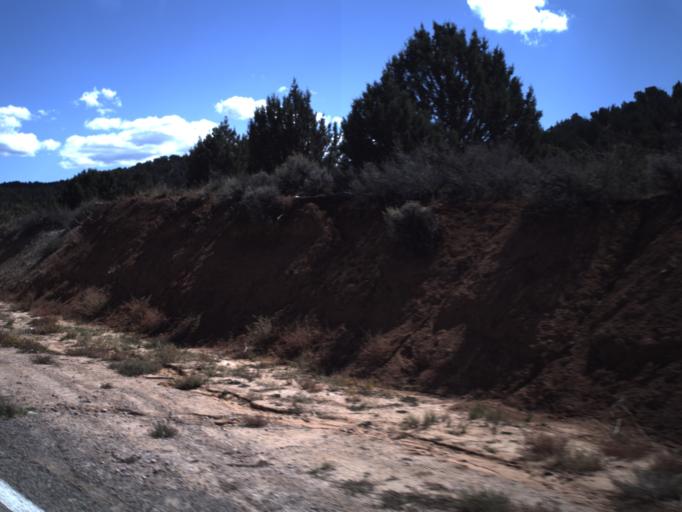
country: US
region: Utah
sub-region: Washington County
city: Enterprise
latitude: 37.5403
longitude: -113.6721
